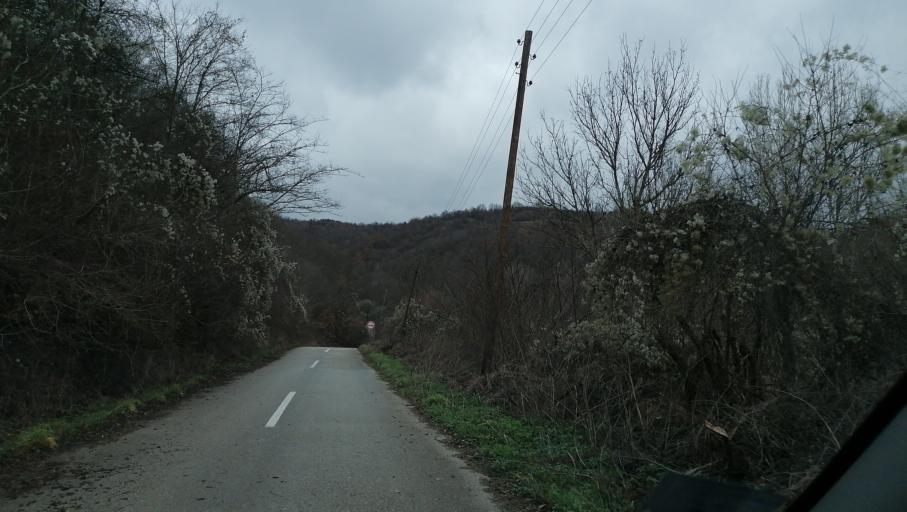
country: RS
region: Central Serbia
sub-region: Pirotski Okrug
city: Dimitrovgrad
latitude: 42.9265
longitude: 22.7563
